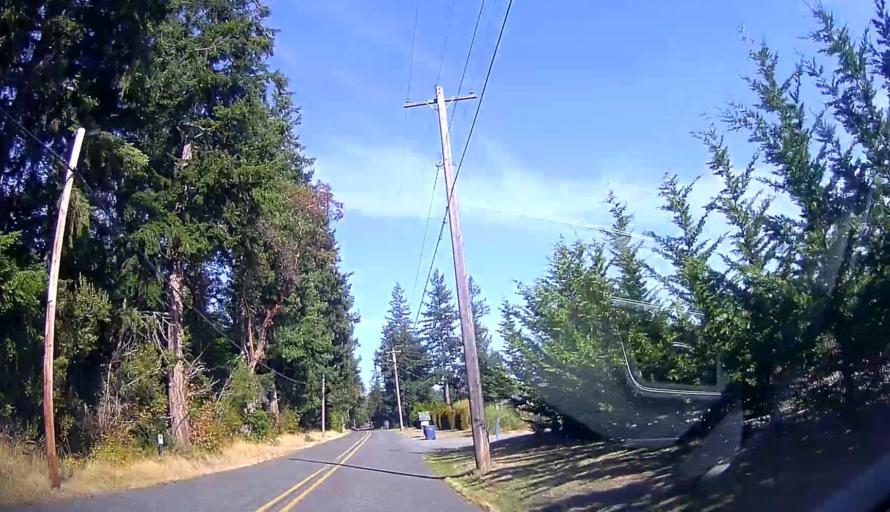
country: US
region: Washington
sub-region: Island County
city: Camano
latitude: 48.1757
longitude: -122.5237
